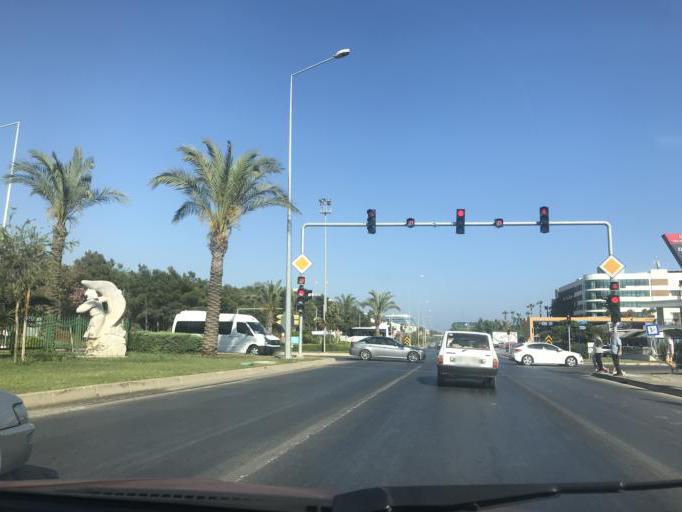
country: TR
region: Antalya
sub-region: Alanya
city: Avsallar
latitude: 36.6089
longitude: 31.7833
